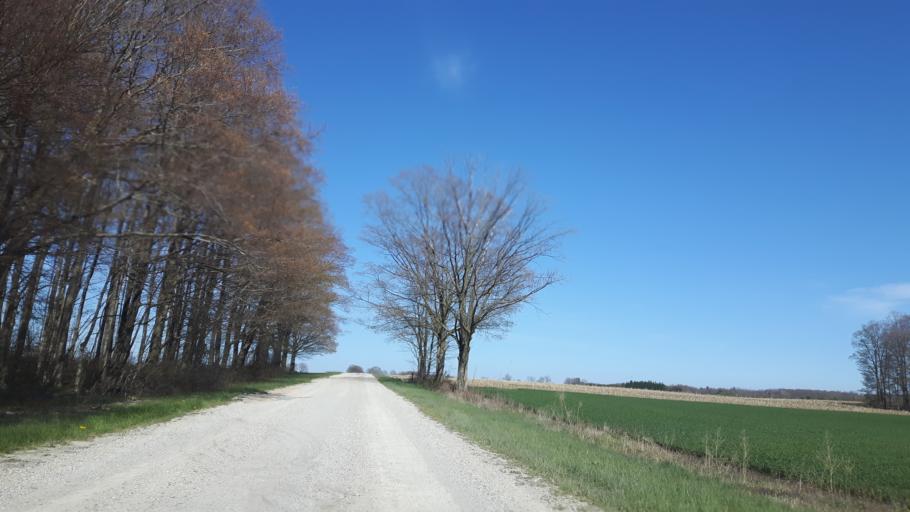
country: CA
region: Ontario
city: Goderich
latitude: 43.6612
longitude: -81.6963
